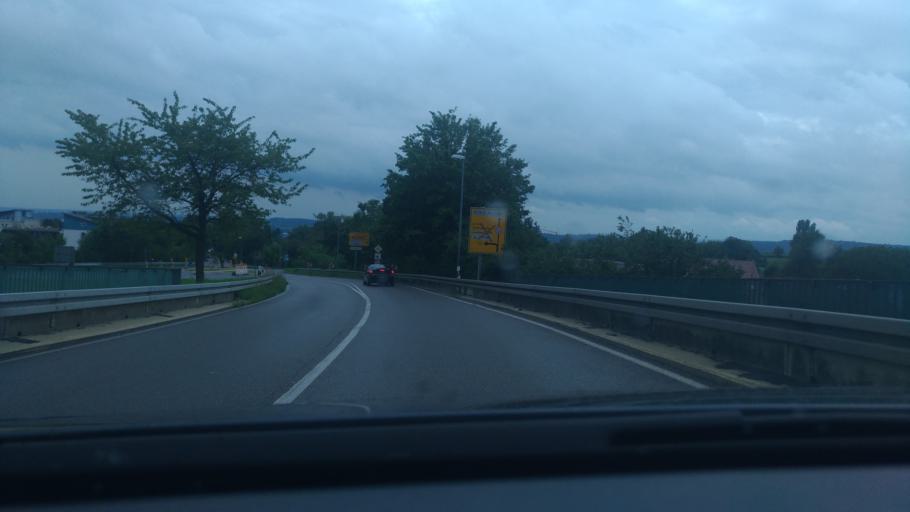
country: DE
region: Baden-Wuerttemberg
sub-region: Tuebingen Region
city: Uberlingen
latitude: 47.7783
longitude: 9.1510
